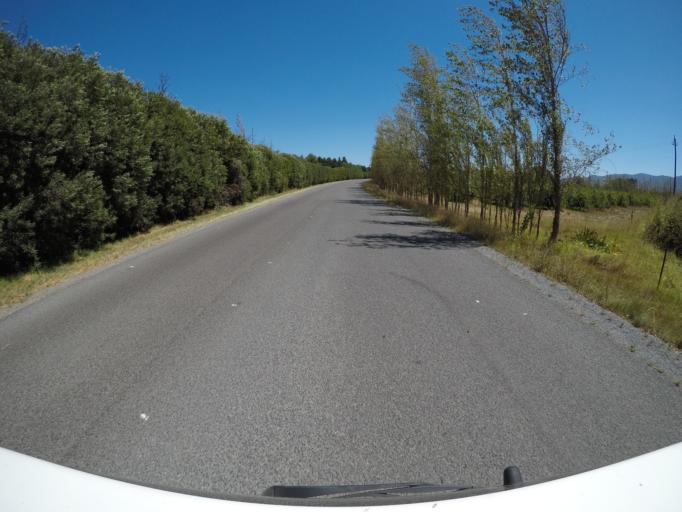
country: ZA
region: Western Cape
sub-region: Overberg District Municipality
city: Grabouw
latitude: -34.1864
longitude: 19.0391
